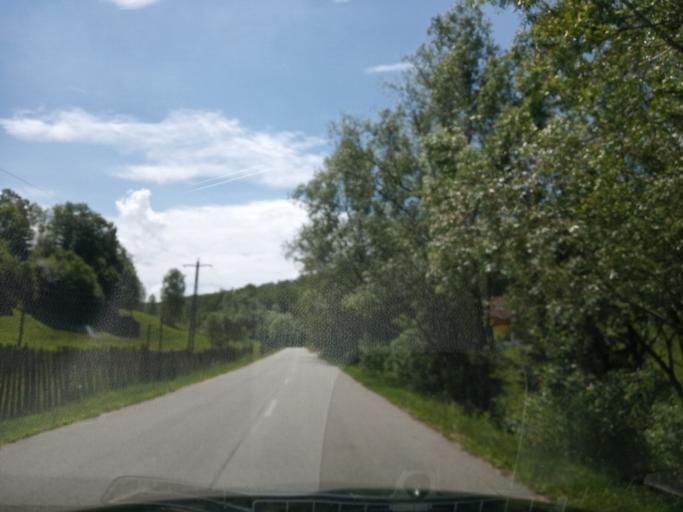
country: RO
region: Hunedoara
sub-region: Oras Petrila
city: Petrila
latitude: 45.4073
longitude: 23.4118
